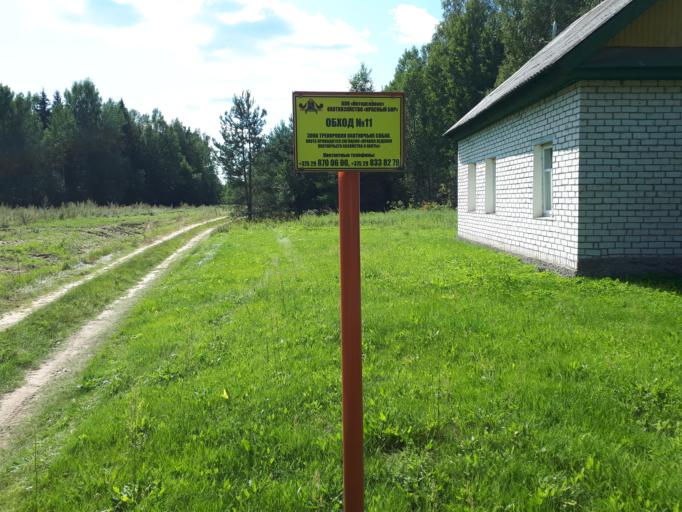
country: BY
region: Vitebsk
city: Rasony
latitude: 55.9882
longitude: 28.5972
